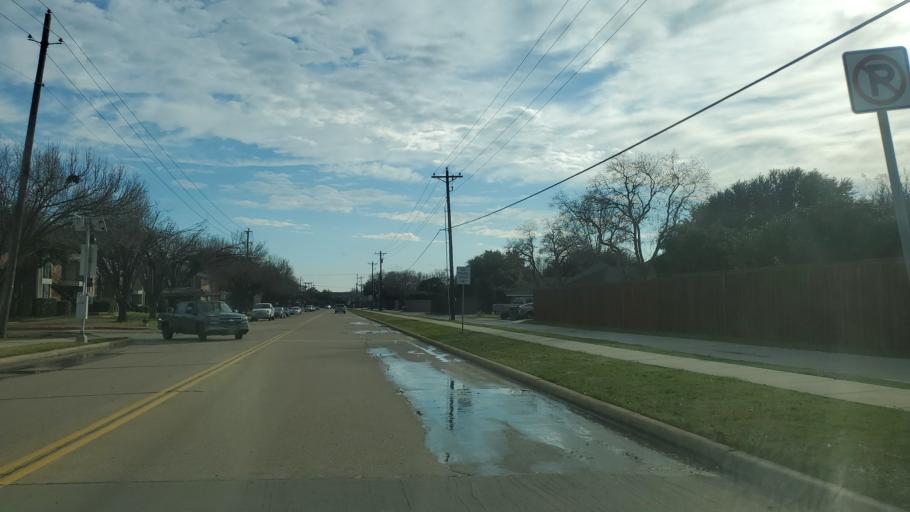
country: US
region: Texas
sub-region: Dallas County
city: Carrollton
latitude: 33.0021
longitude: -96.8985
